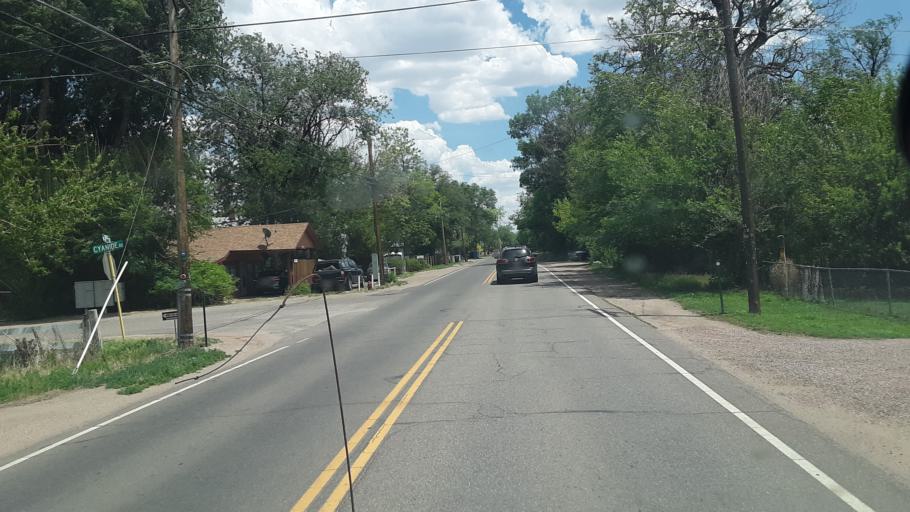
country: US
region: Colorado
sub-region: Fremont County
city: Florence
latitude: 38.3999
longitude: -105.1334
